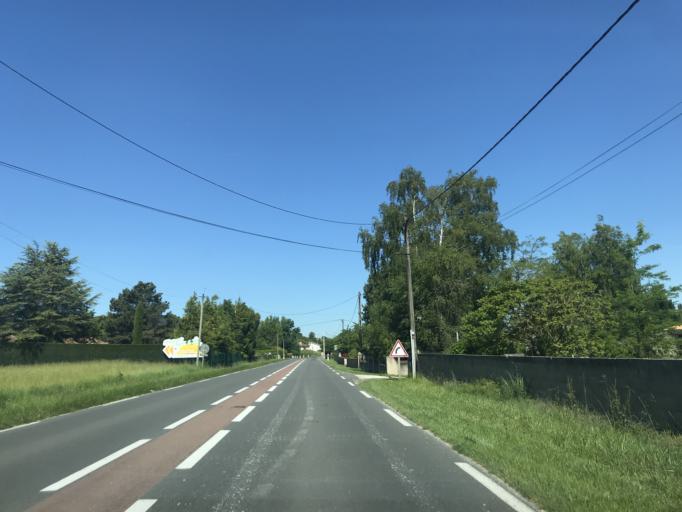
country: FR
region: Poitou-Charentes
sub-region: Departement de la Charente
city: Barbezieux-Saint-Hilaire
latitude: 45.4821
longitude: -0.1779
